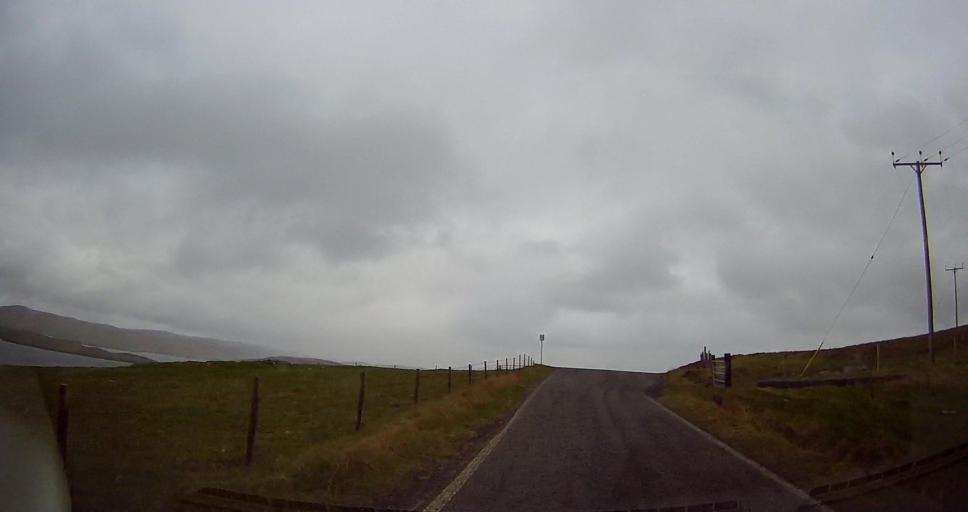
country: GB
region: Scotland
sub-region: Shetland Islands
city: Lerwick
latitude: 60.3816
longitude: -1.3792
